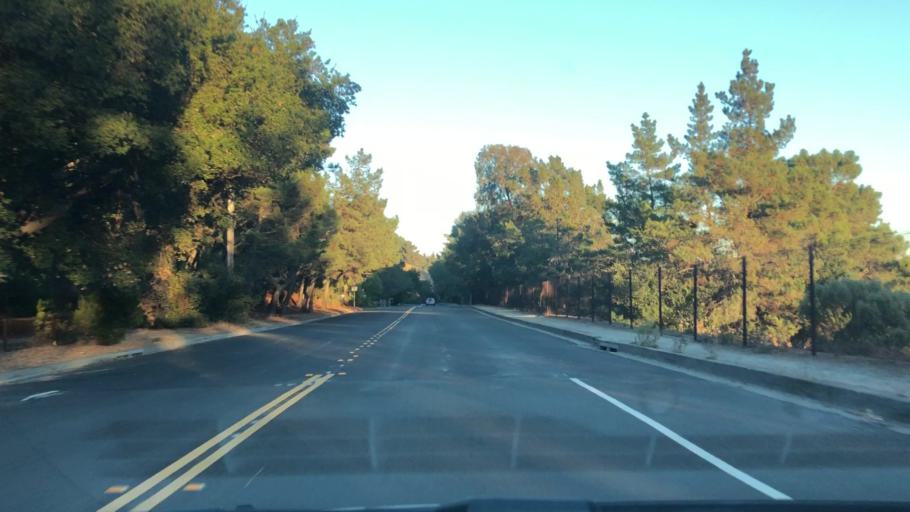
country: US
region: California
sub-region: Contra Costa County
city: Orinda
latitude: 37.8936
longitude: -122.1651
